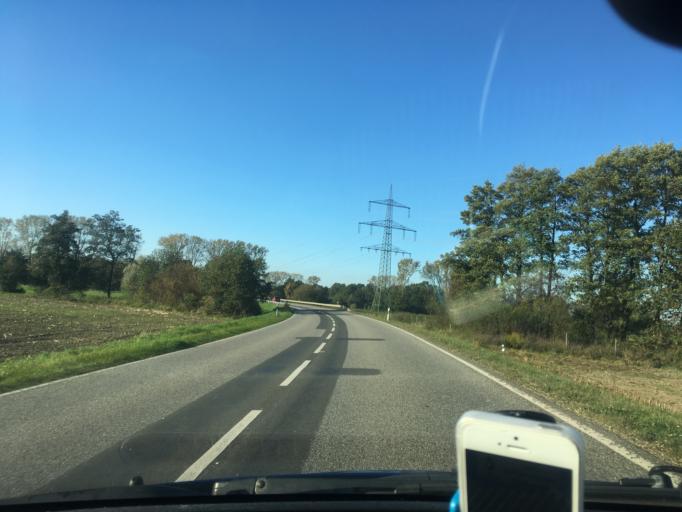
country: DE
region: Mecklenburg-Vorpommern
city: Wittenburg
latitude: 53.5177
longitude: 11.0858
